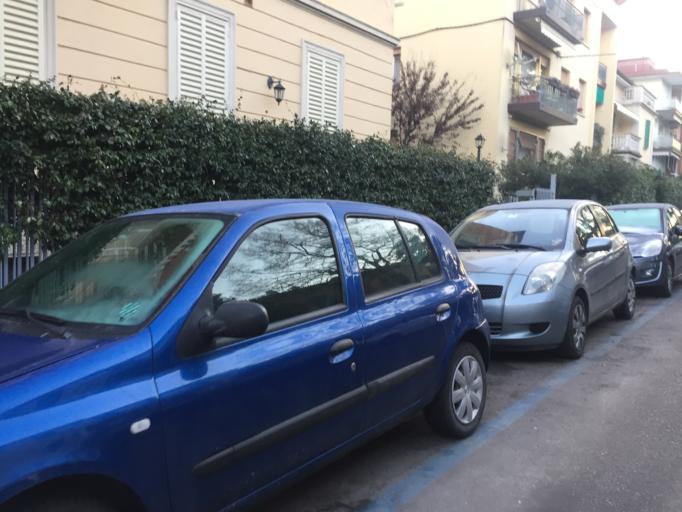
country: IT
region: Emilia-Romagna
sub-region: Provincia di Bologna
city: Bologna
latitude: 44.4932
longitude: 11.3236
